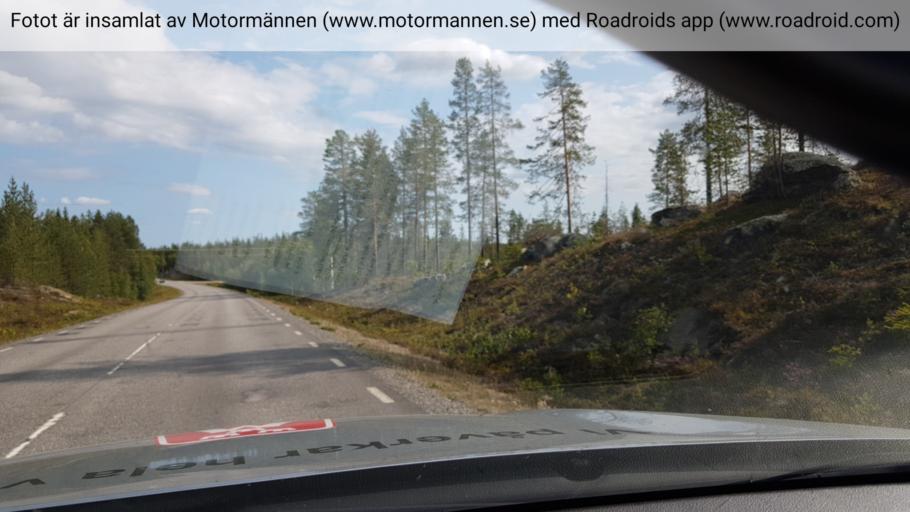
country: SE
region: Vaesterbotten
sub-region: Skelleftea Kommun
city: Storvik
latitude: 65.3312
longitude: 20.5914
